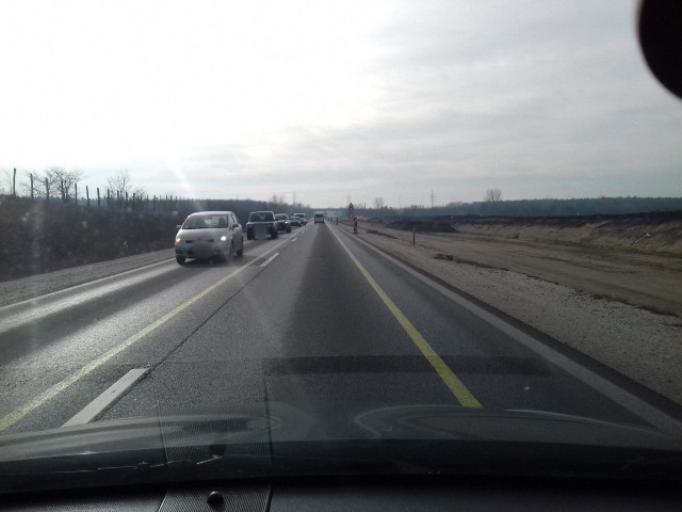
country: HU
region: Pest
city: God
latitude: 47.6721
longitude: 19.1686
